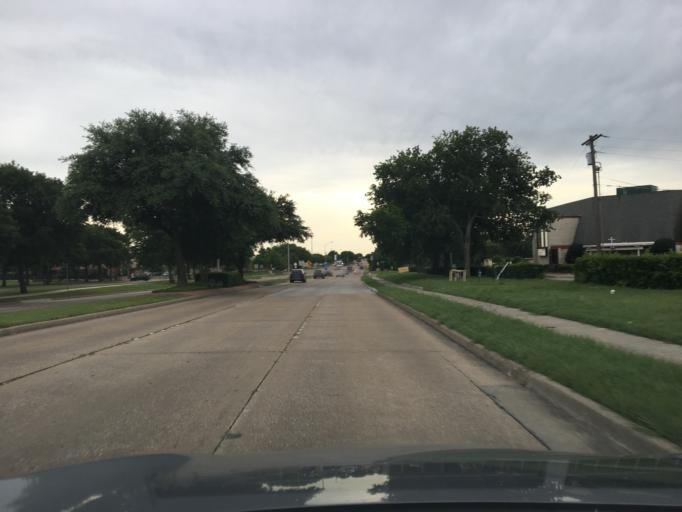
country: US
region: Texas
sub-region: Dallas County
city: Richardson
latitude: 32.9506
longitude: -96.7000
